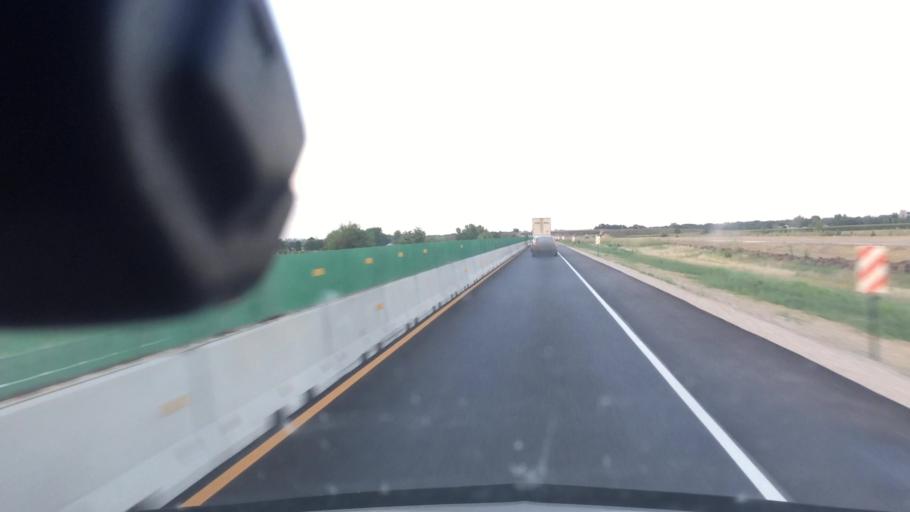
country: US
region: Illinois
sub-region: Livingston County
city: Pontiac
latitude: 40.9386
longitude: -88.6004
